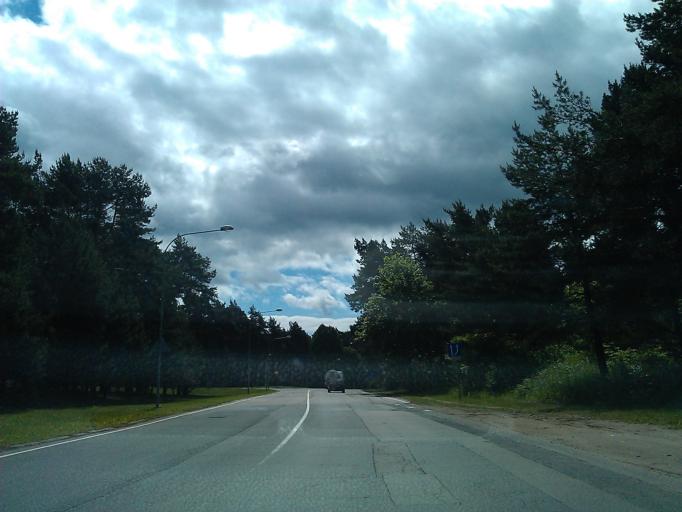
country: LV
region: Babite
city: Pinki
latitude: 56.9699
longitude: 23.8645
